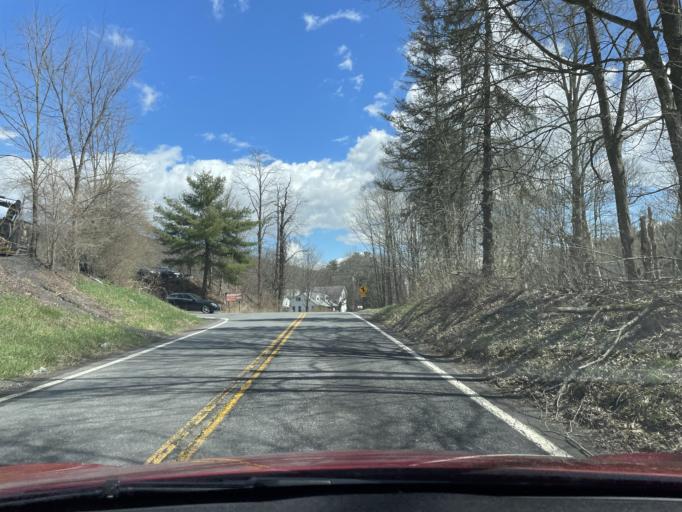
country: US
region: New York
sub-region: Ulster County
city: West Hurley
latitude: 41.9721
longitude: -74.0803
